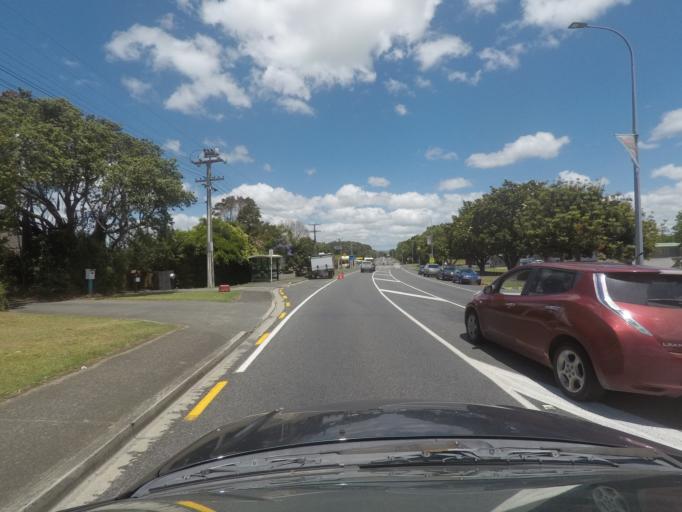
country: NZ
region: Northland
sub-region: Whangarei
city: Whangarei
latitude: -35.7559
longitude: 174.3686
